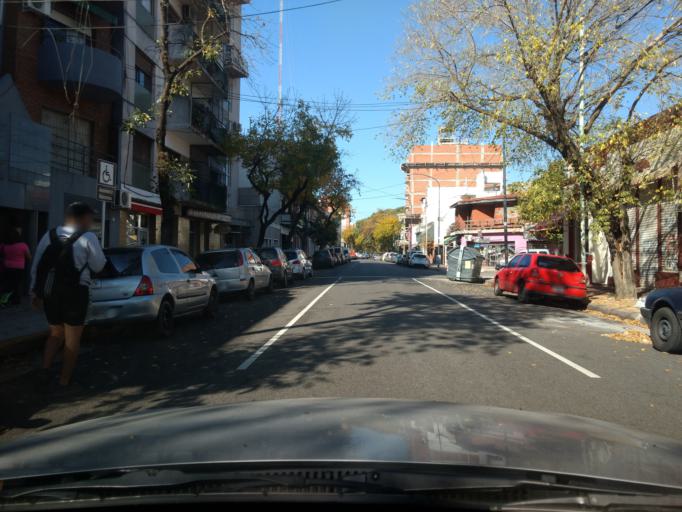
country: AR
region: Buenos Aires F.D.
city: Villa Santa Rita
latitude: -34.6378
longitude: -58.4844
